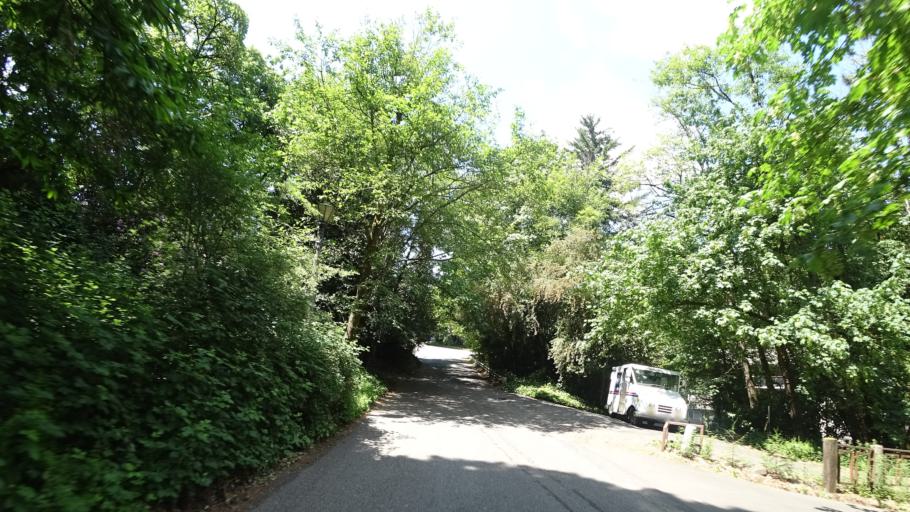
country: US
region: Oregon
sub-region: Multnomah County
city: Portland
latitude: 45.4788
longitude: -122.6912
